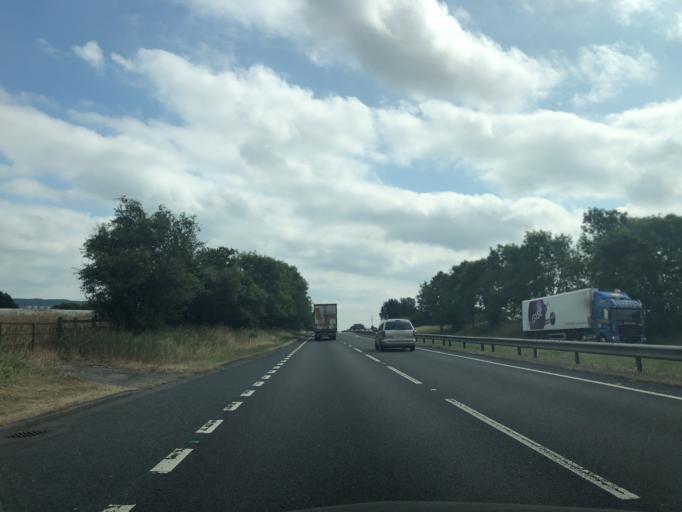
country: GB
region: England
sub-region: Stockton-on-Tees
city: Yarm
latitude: 54.4226
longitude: -1.3201
